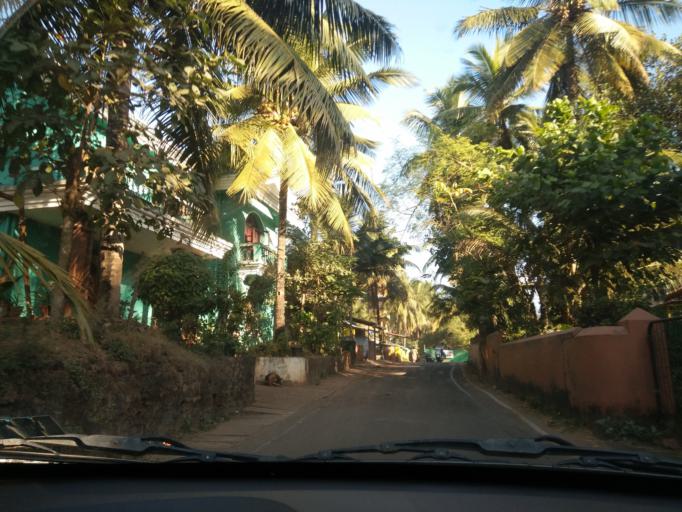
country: IN
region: Goa
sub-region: South Goa
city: Madgaon
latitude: 15.2643
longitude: 73.9582
